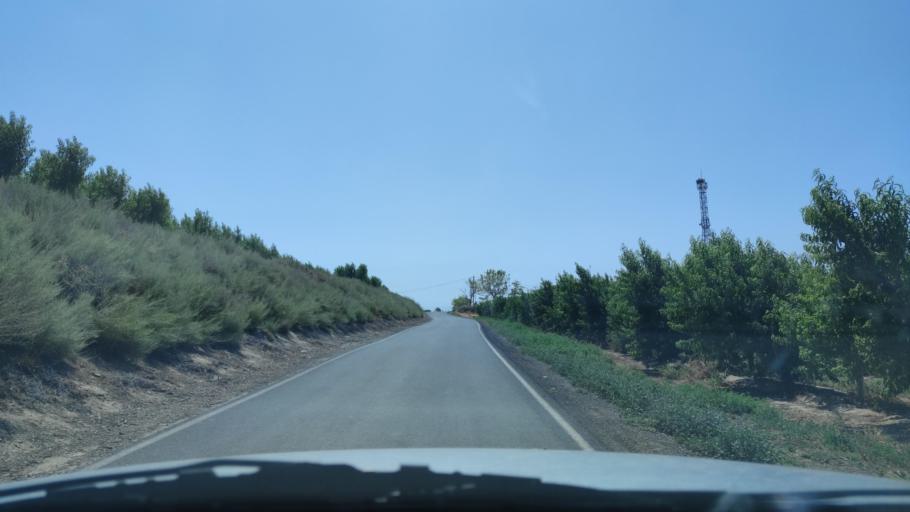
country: ES
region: Catalonia
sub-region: Provincia de Lleida
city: Alpicat
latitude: 41.6687
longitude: 0.5687
